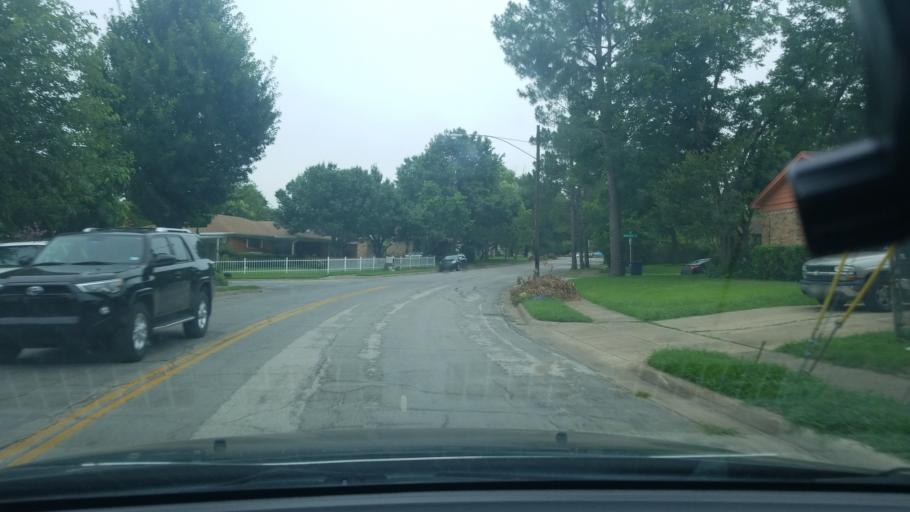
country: US
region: Texas
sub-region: Dallas County
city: Balch Springs
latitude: 32.7592
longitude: -96.6728
